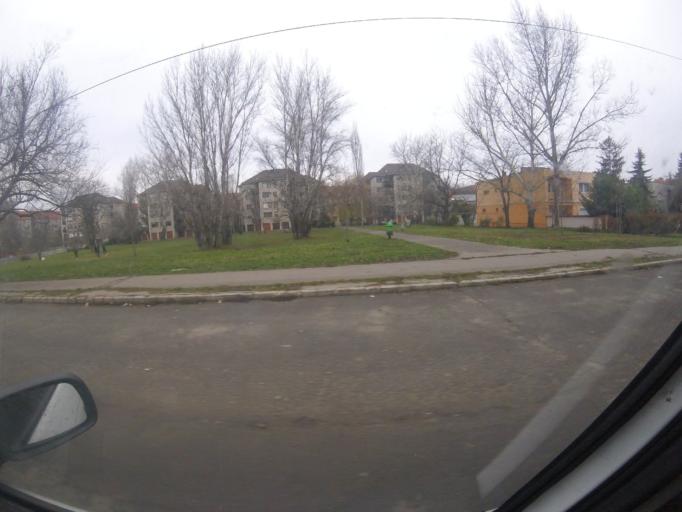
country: HU
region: Budapest
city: Budapest III. keruelet
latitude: 47.5660
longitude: 19.0560
